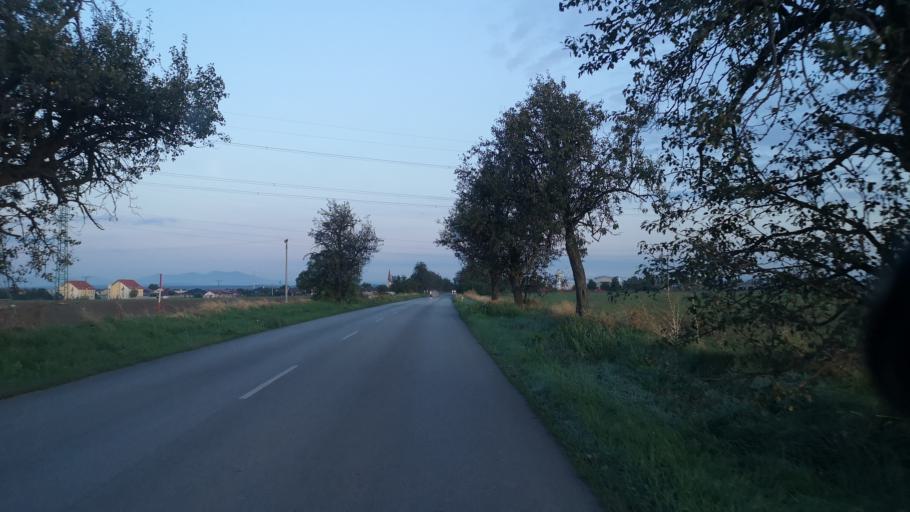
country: SK
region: Trnavsky
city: Leopoldov
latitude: 48.4467
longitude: 17.6859
